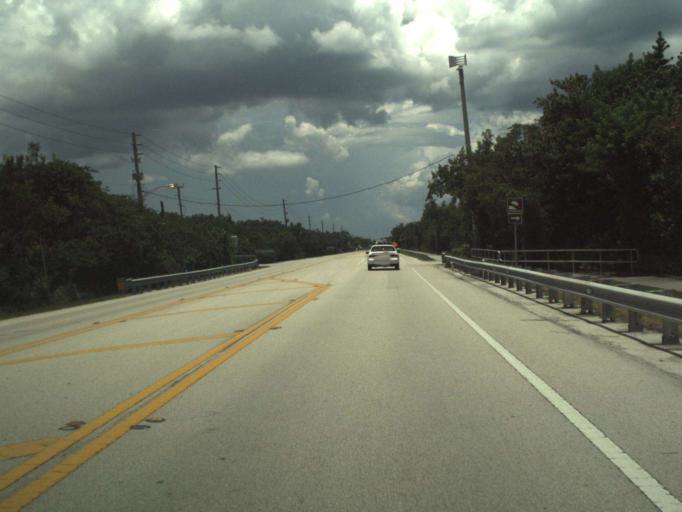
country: US
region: Florida
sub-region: Martin County
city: Sewall's Point
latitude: 27.2369
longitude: -80.1875
